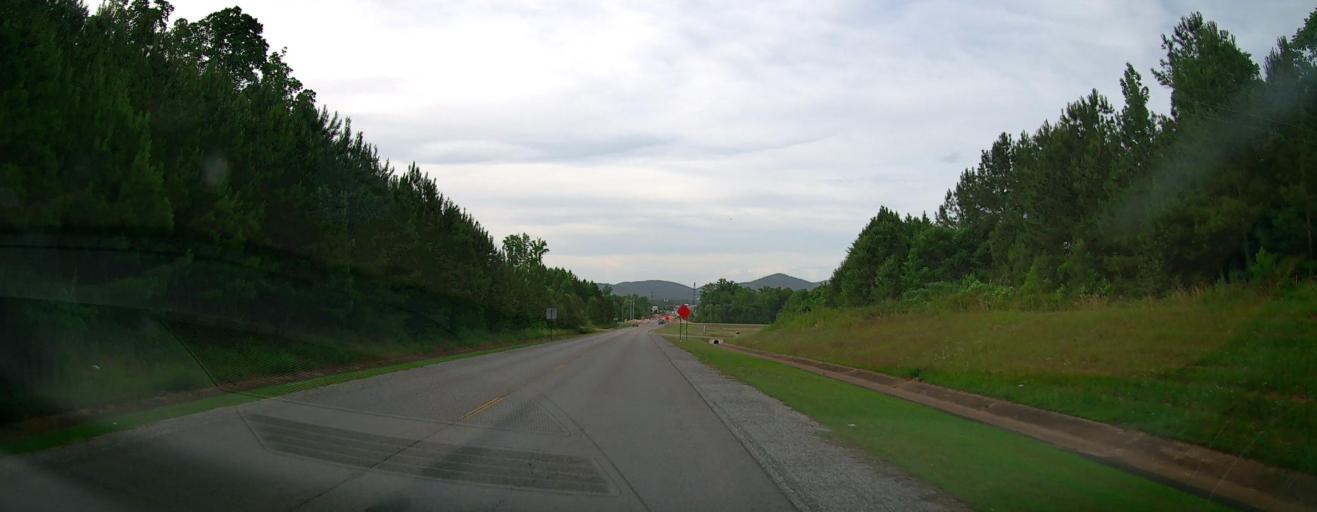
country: US
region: Alabama
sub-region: Calhoun County
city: Oxford
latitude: 33.5970
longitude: -85.7858
